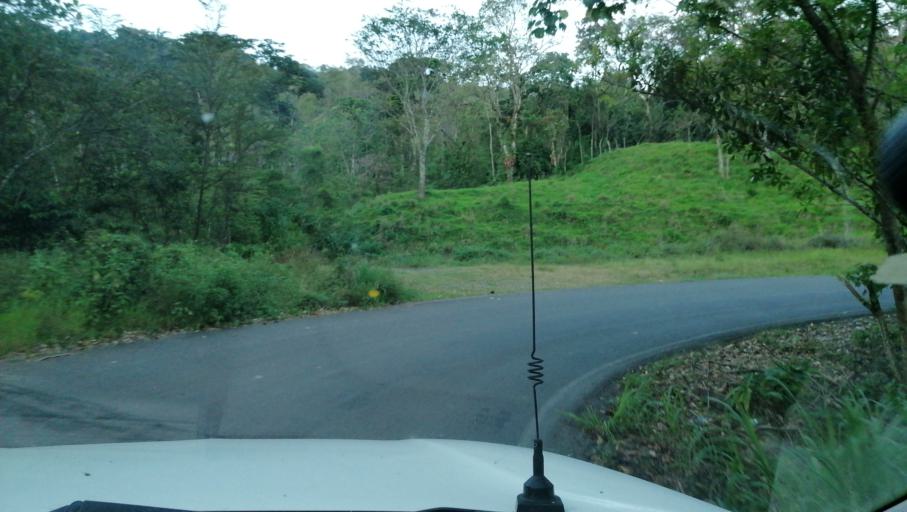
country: MX
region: Chiapas
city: Ostuacan
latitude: 17.4235
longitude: -93.3381
